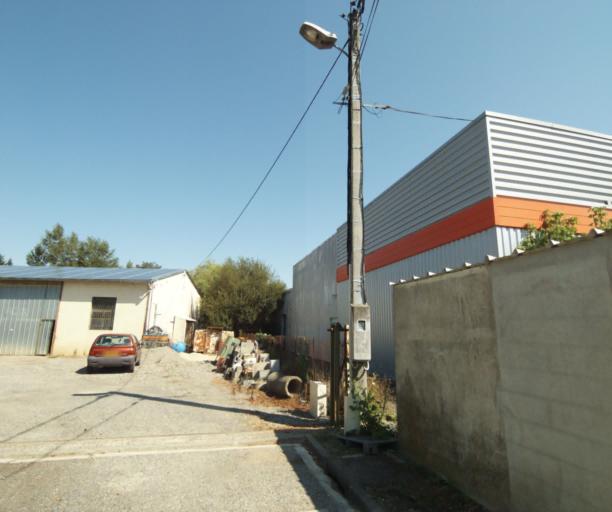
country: FR
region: Midi-Pyrenees
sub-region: Departement de l'Ariege
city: Lezat-sur-Leze
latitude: 43.2821
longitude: 1.3482
